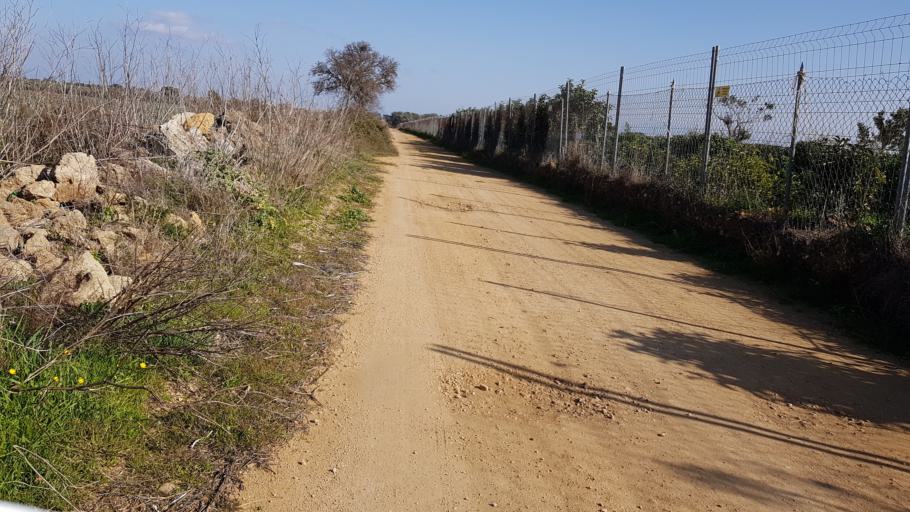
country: IT
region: Apulia
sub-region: Provincia di Brindisi
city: Mesagne
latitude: 40.5900
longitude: 17.8663
